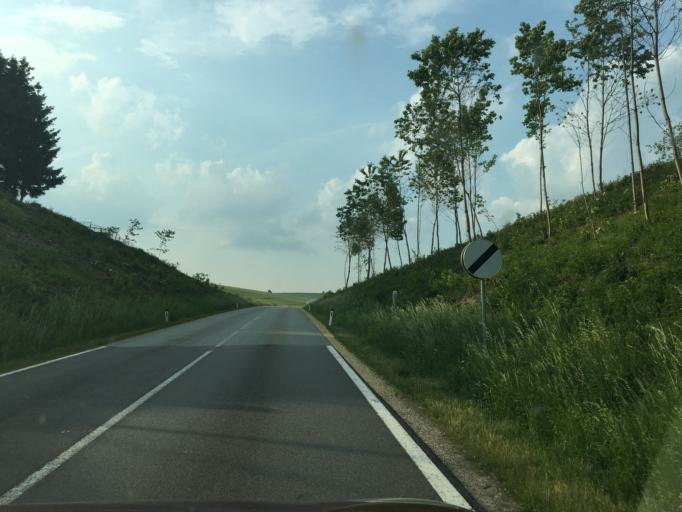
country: AT
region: Upper Austria
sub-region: Politischer Bezirk Ried im Innkreis
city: Ried im Innkreis
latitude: 48.1841
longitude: 13.5760
